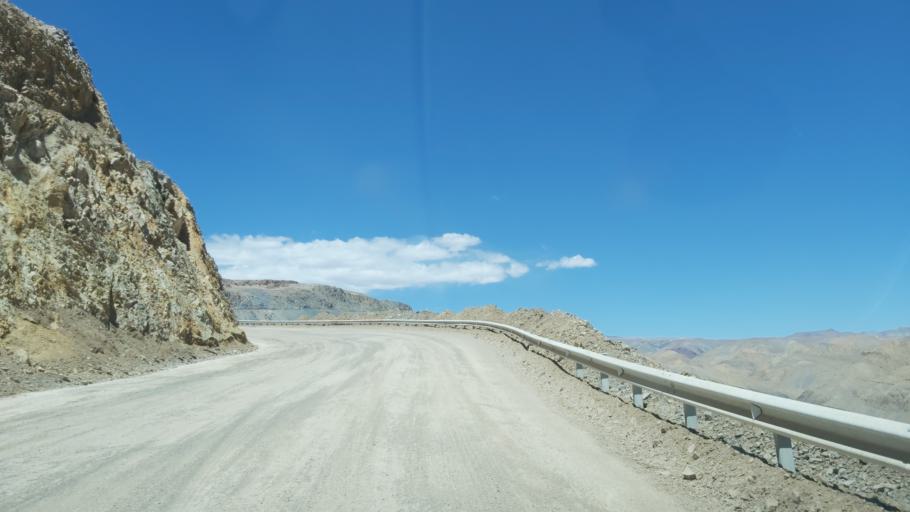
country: CL
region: Atacama
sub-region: Provincia de Chanaral
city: Diego de Almagro
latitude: -26.4553
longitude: -69.3146
